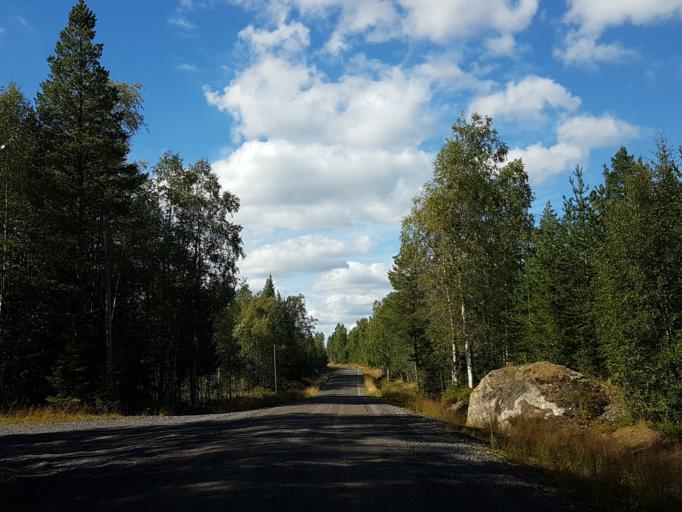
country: SE
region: Vaesterbotten
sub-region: Skelleftea Kommun
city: Burtraesk
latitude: 64.2803
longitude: 20.4697
